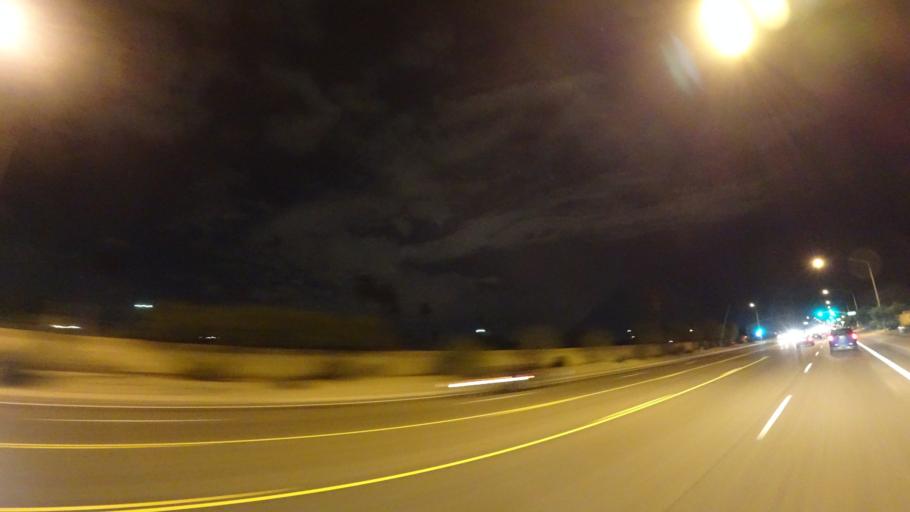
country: US
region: Arizona
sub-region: Maricopa County
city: San Carlos
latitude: 33.3601
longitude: -111.8767
